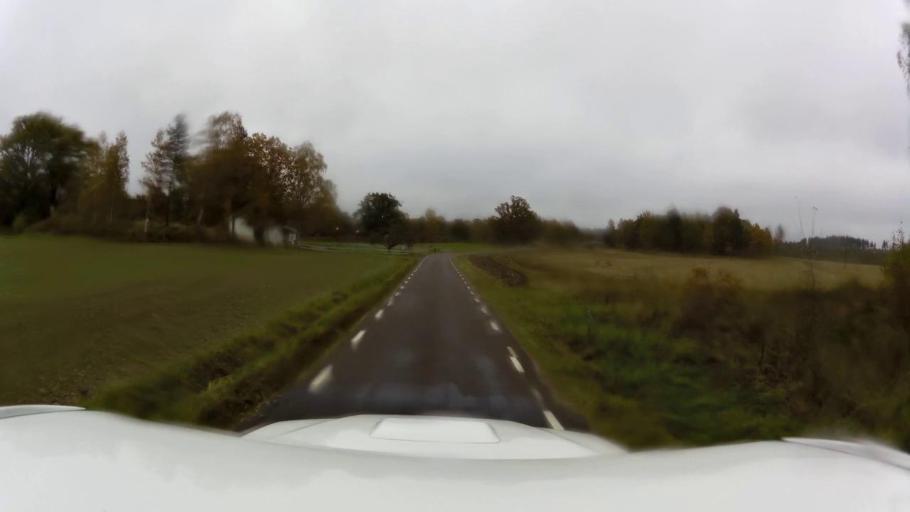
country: SE
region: OEstergoetland
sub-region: Linkopings Kommun
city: Linghem
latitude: 58.3519
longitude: 15.8760
